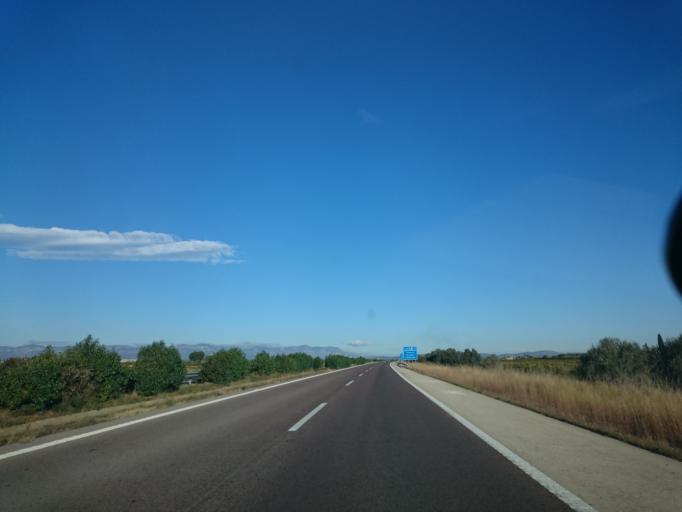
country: ES
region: Valencia
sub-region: Provincia de Castello
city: Vinaros
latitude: 40.5090
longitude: 0.4155
